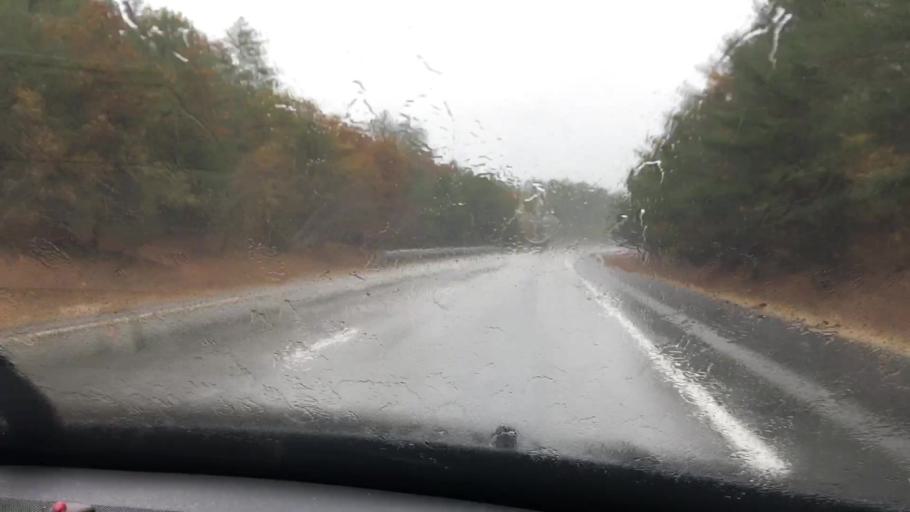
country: US
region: New Hampshire
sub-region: Merrimack County
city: Boscawen
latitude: 43.3167
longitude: -71.5904
